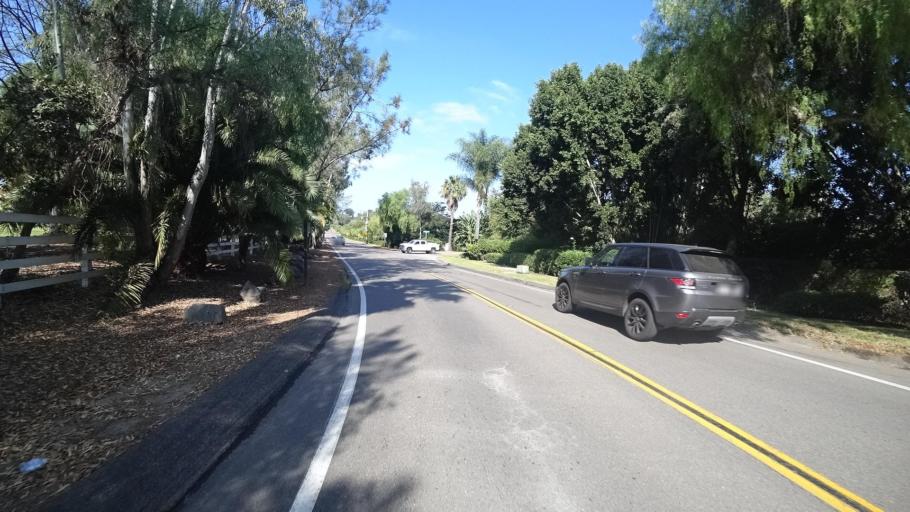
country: US
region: California
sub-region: San Diego County
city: Rancho Santa Fe
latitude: 33.0435
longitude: -117.1866
